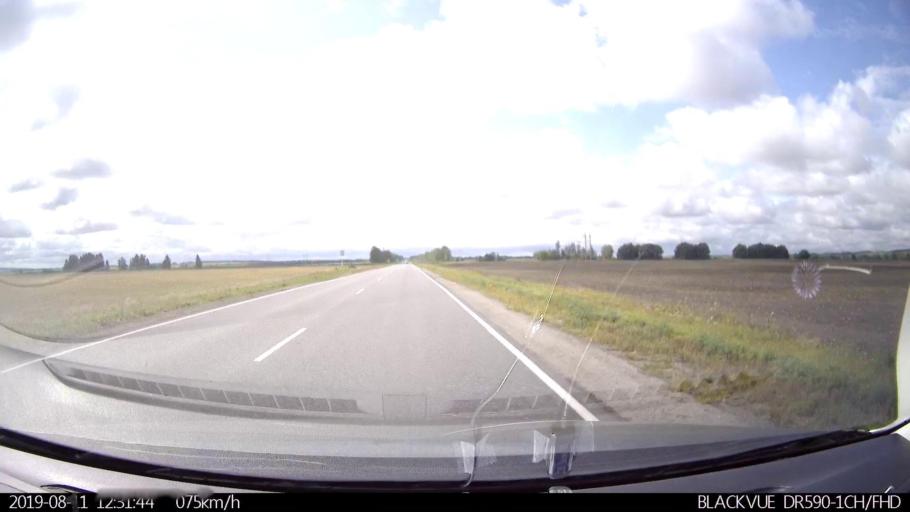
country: RU
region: Ulyanovsk
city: Ignatovka
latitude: 53.8176
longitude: 47.8803
